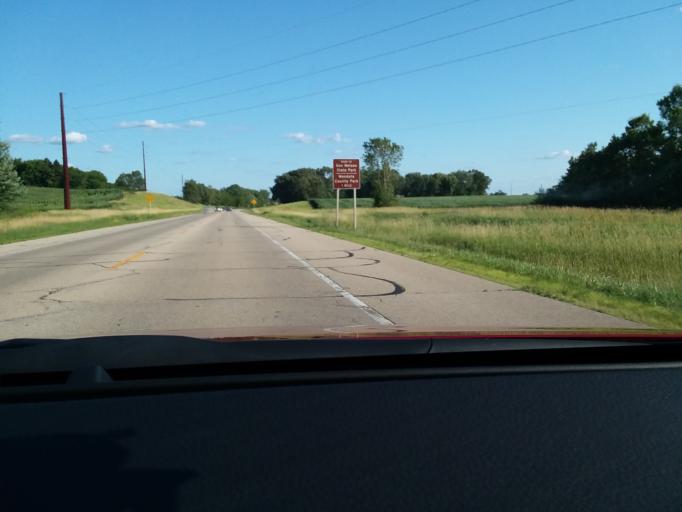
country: US
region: Wisconsin
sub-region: Dane County
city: Waunakee
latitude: 43.1671
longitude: -89.4085
